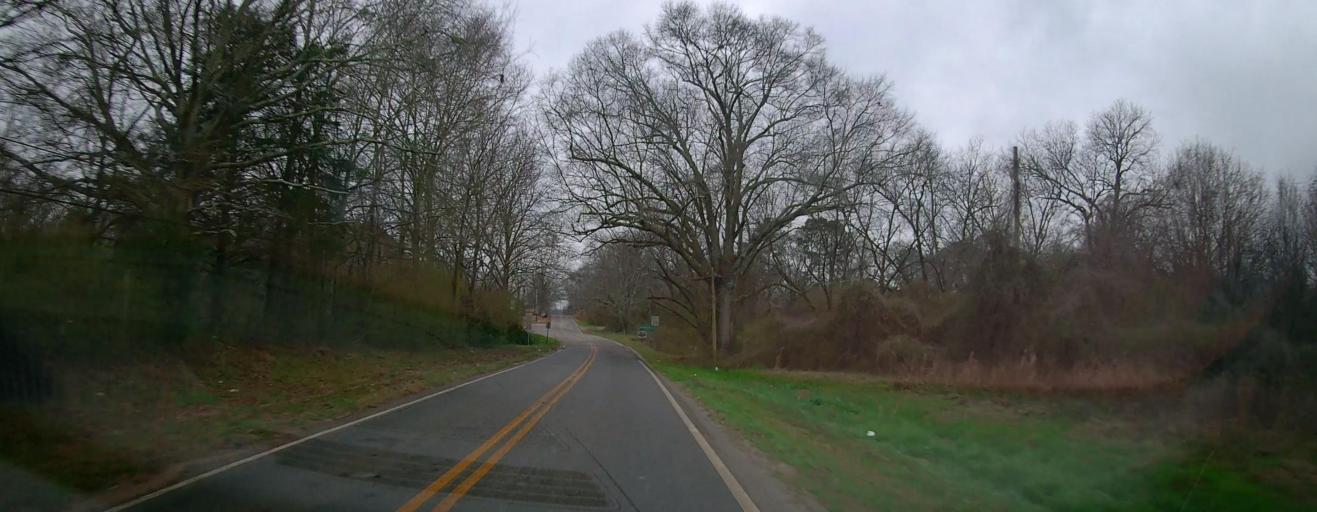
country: US
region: Georgia
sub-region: Lamar County
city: Barnesville
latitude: 33.0629
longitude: -84.1418
